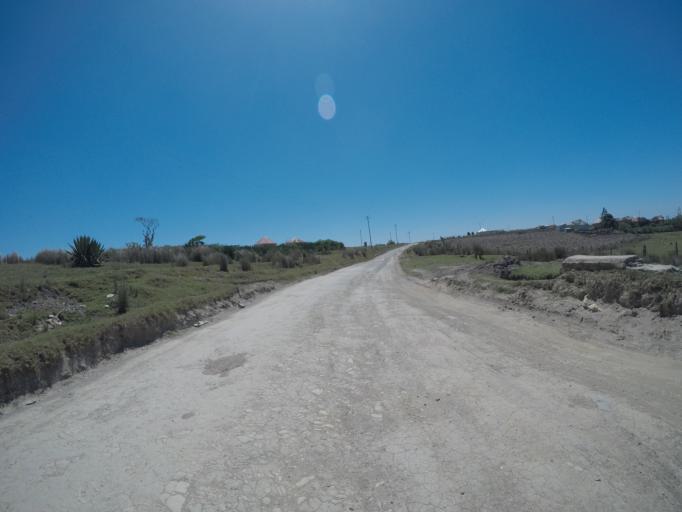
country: ZA
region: Eastern Cape
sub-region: OR Tambo District Municipality
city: Libode
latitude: -31.9472
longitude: 29.0253
